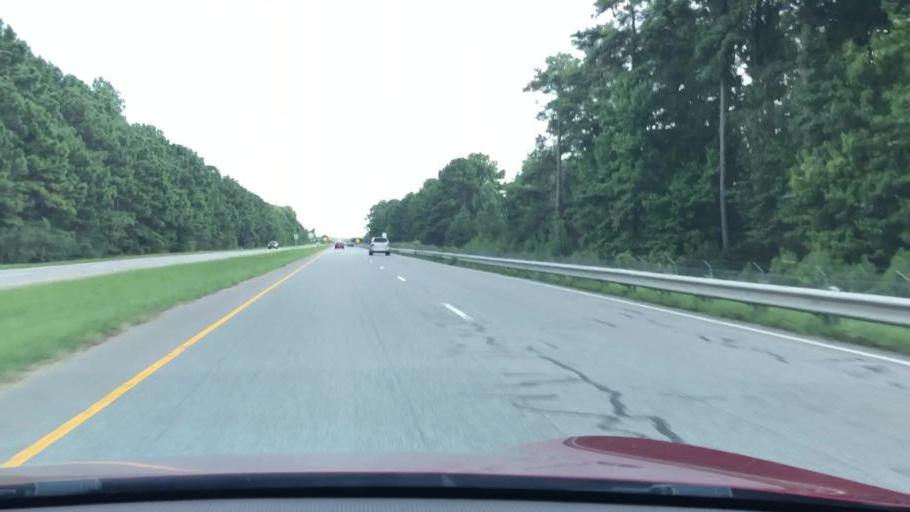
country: US
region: Virginia
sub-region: City of Virginia Beach
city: Virginia Beach
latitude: 36.8334
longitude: -76.0121
